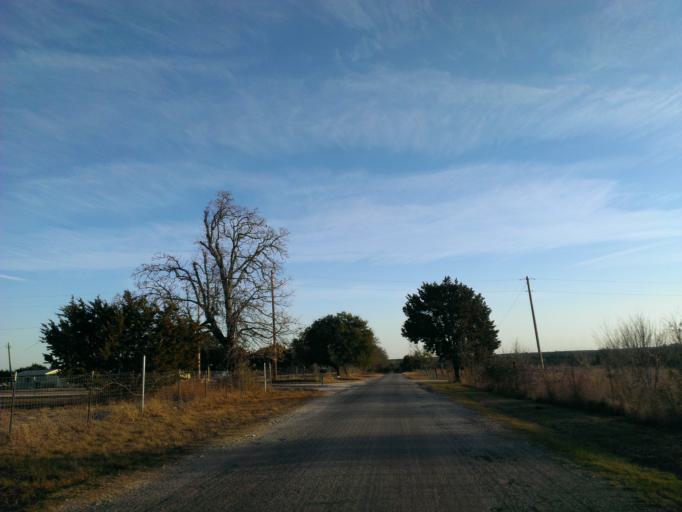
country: US
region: Texas
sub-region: Burnet County
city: Bertram
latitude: 30.7271
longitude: -98.0809
